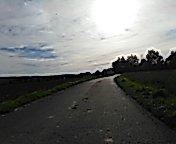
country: LU
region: Luxembourg
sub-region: Canton de Capellen
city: Steinfort
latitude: 49.6404
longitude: 5.9196
